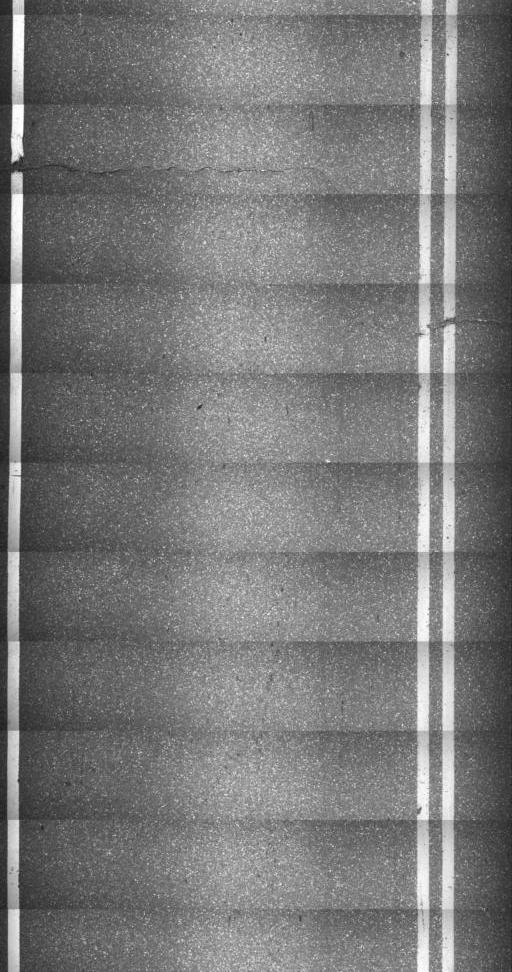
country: US
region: Vermont
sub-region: Washington County
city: Northfield
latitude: 44.1467
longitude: -72.6564
